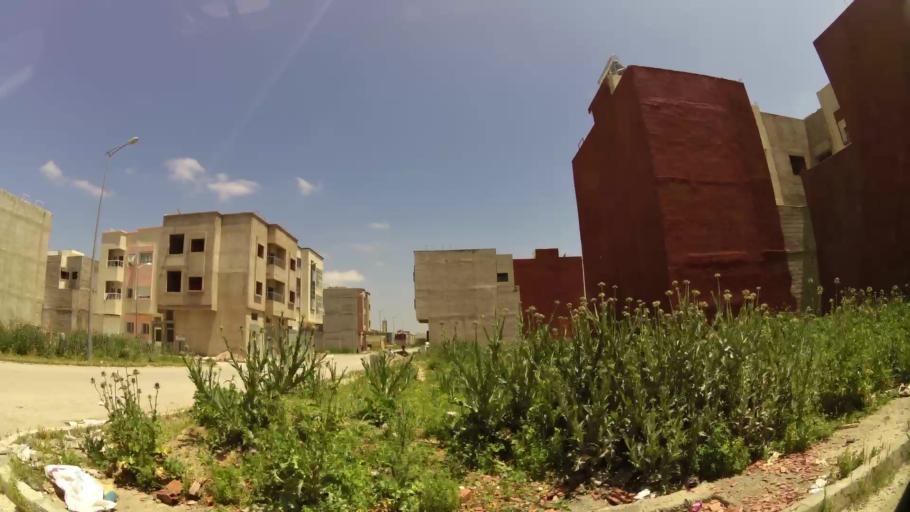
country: MA
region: Fes-Boulemane
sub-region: Fes
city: Fes
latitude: 34.0345
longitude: -5.0542
